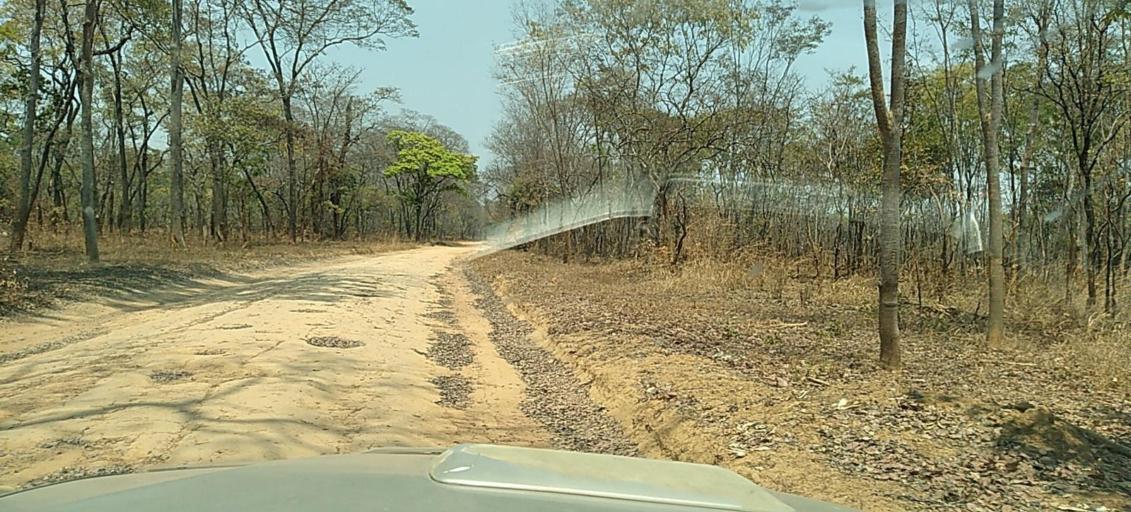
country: ZM
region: North-Western
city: Kasempa
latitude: -13.6159
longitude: 26.2002
